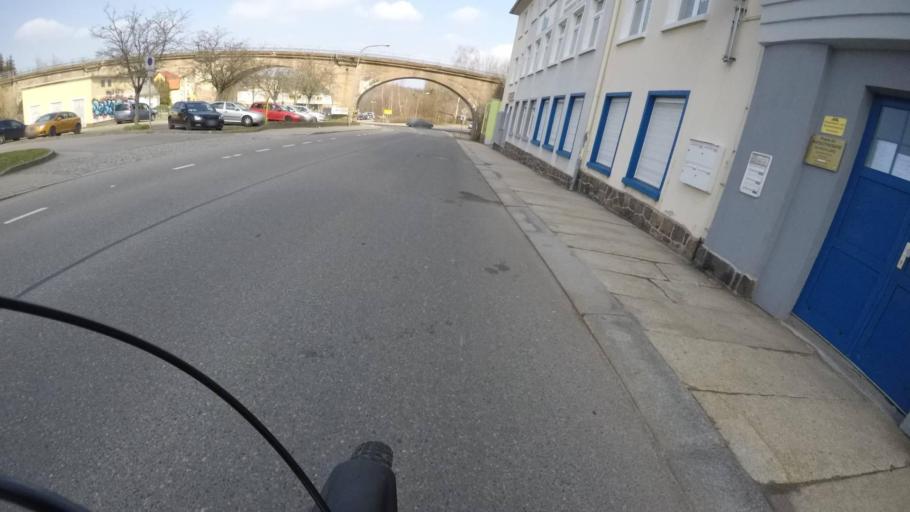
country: DE
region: Saxony
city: Limbach-Oberfrohna
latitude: 50.8612
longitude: 12.7612
